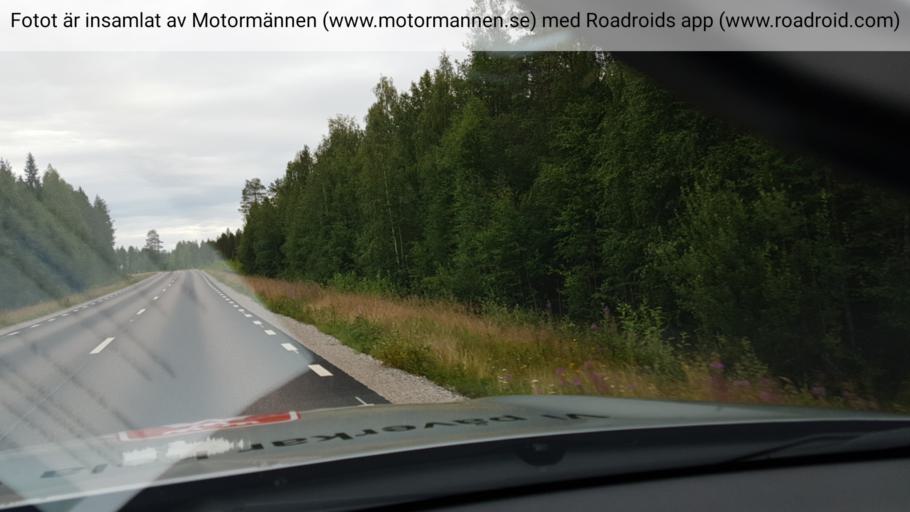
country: SE
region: Norrbotten
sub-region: Overkalix Kommun
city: OEverkalix
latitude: 66.4081
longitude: 22.8059
